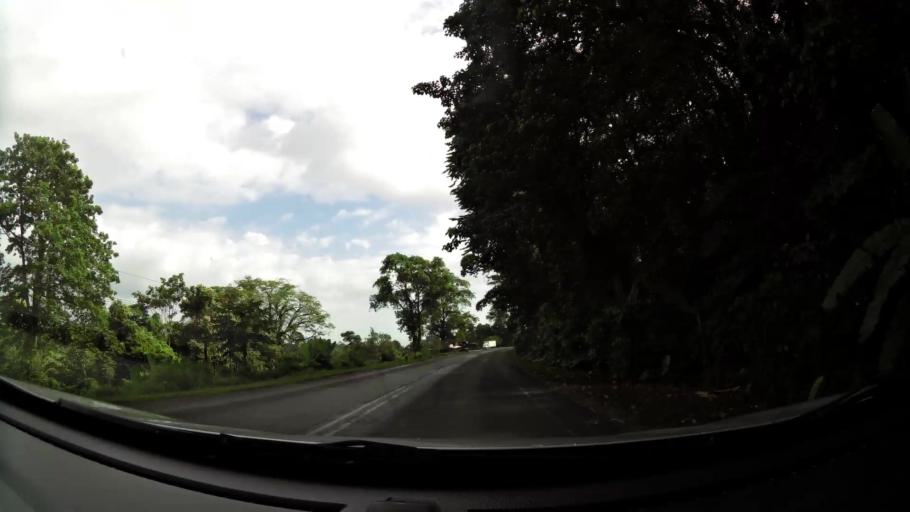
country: CR
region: Limon
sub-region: Canton de Siquirres
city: Pacuarito
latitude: 10.1005
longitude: -83.4750
